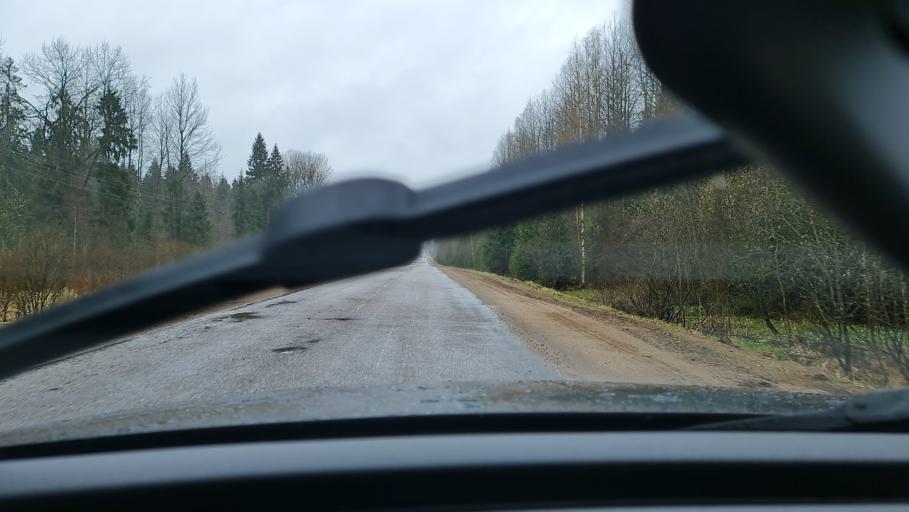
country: RU
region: Novgorod
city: Kresttsy
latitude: 58.0280
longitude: 32.8103
